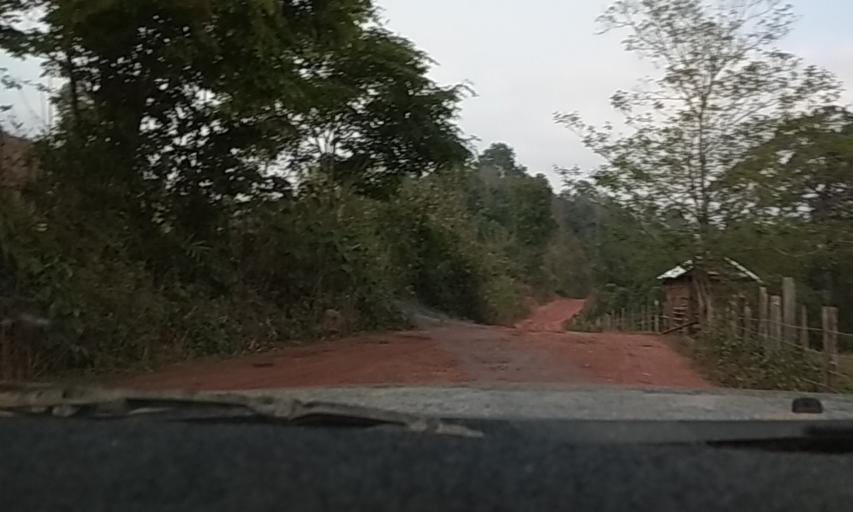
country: TH
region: Nan
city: Mae Charim
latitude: 18.4460
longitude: 101.1917
